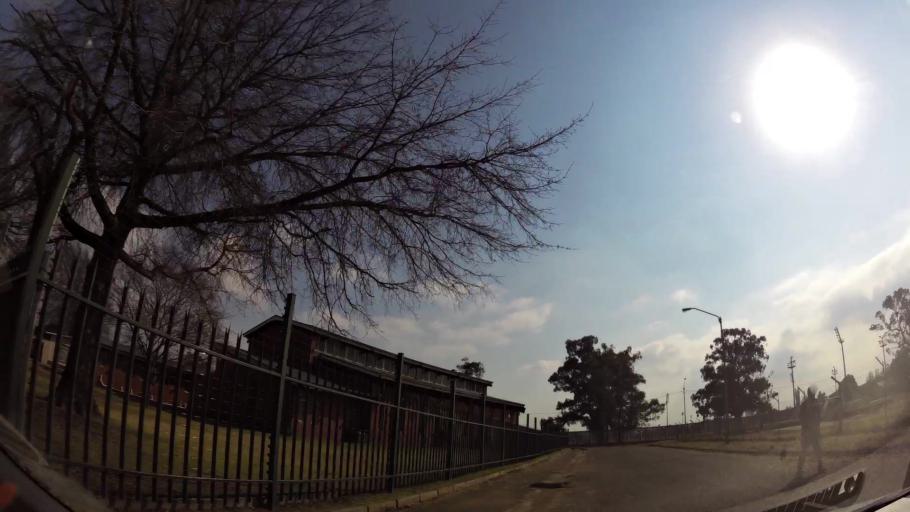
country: ZA
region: Gauteng
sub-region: Ekurhuleni Metropolitan Municipality
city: Boksburg
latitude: -26.1616
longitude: 28.2024
